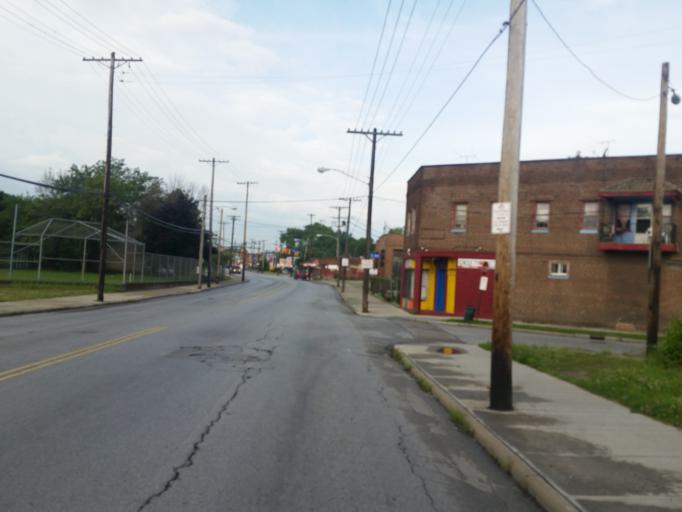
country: US
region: Ohio
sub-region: Cuyahoga County
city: East Cleveland
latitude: 41.5513
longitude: -81.5825
